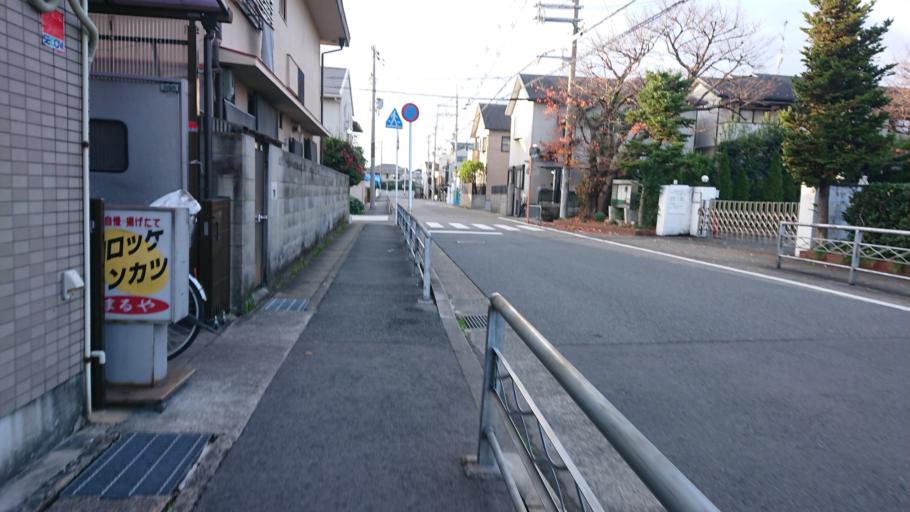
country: JP
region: Kyoto
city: Muko
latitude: 34.9778
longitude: 135.6995
